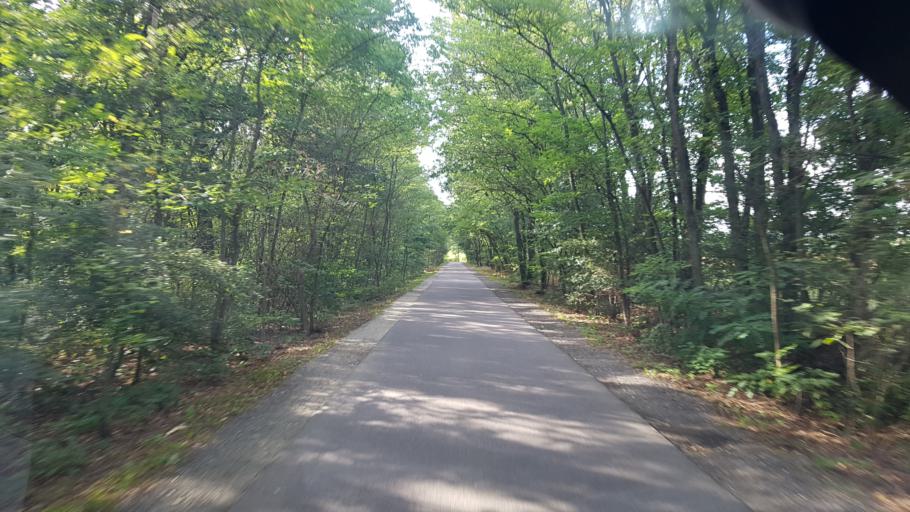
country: DE
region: Brandenburg
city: Spremberg
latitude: 51.5495
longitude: 14.3269
